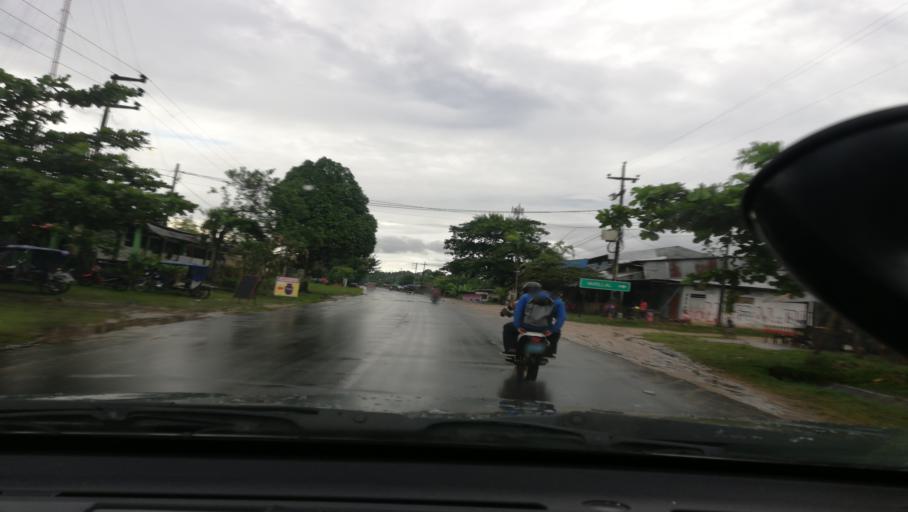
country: PE
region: Loreto
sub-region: Provincia de Maynas
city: Iquitos
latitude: -3.8871
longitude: -73.3516
